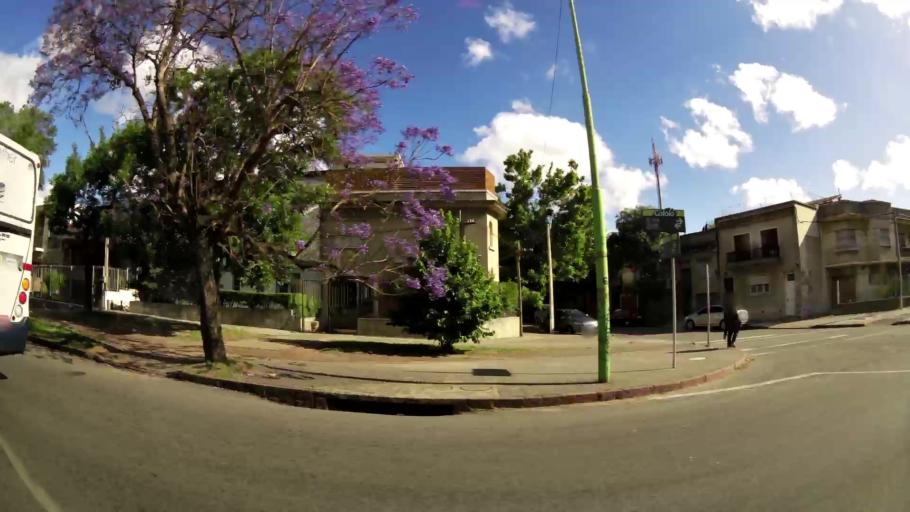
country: UY
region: Montevideo
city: Montevideo
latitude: -34.8721
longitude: -56.1987
